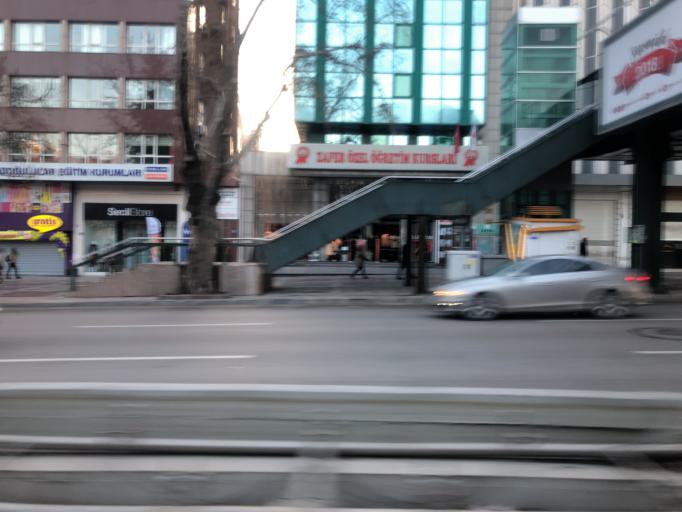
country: TR
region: Ankara
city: Ankara
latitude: 39.9163
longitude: 32.8541
